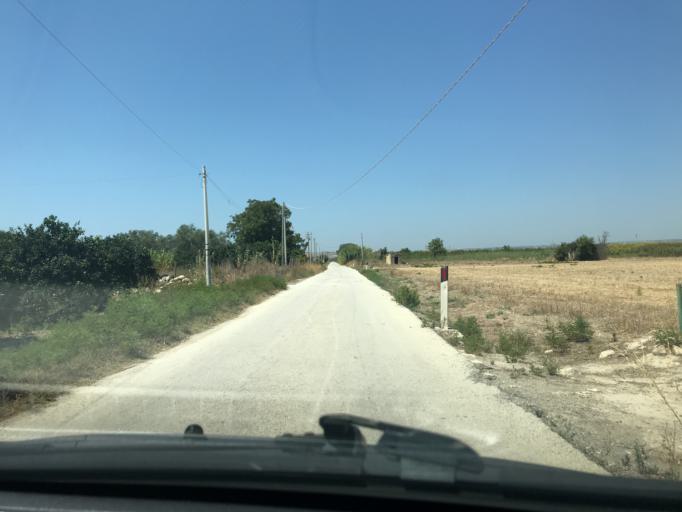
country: IT
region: Sicily
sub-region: Provincia di Siracusa
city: Noto
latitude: 36.8354
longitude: 15.0516
